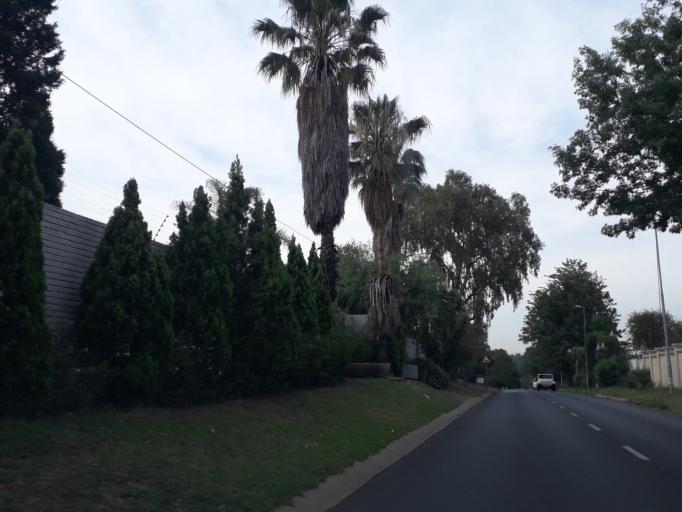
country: ZA
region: Gauteng
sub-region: City of Johannesburg Metropolitan Municipality
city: Modderfontein
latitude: -26.0787
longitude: 28.0440
